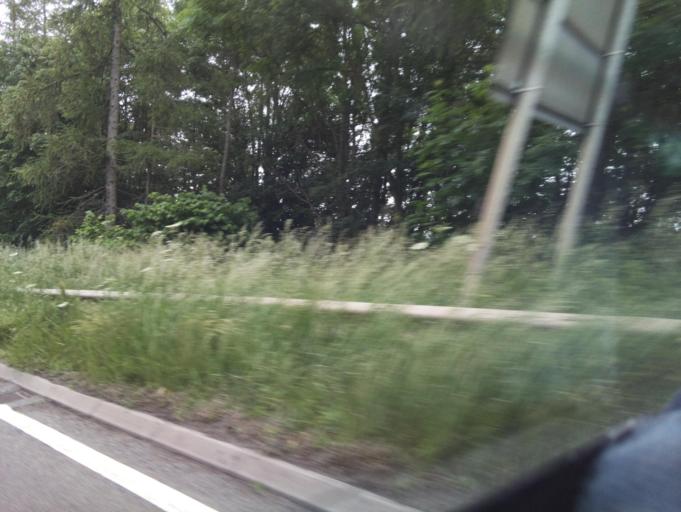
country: GB
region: England
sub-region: Leicestershire
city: Houghton on the Hill
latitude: 52.6203
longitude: -0.9276
